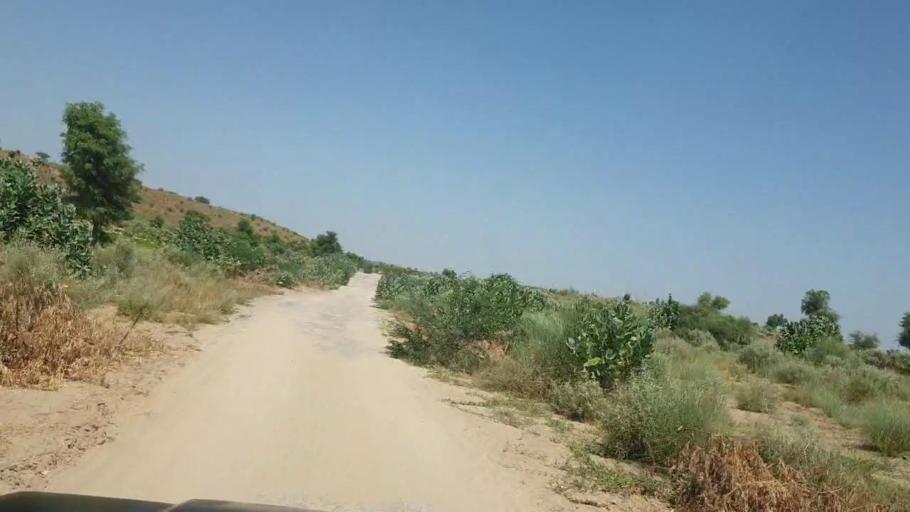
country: PK
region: Sindh
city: Chor
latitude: 25.3862
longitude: 70.3123
